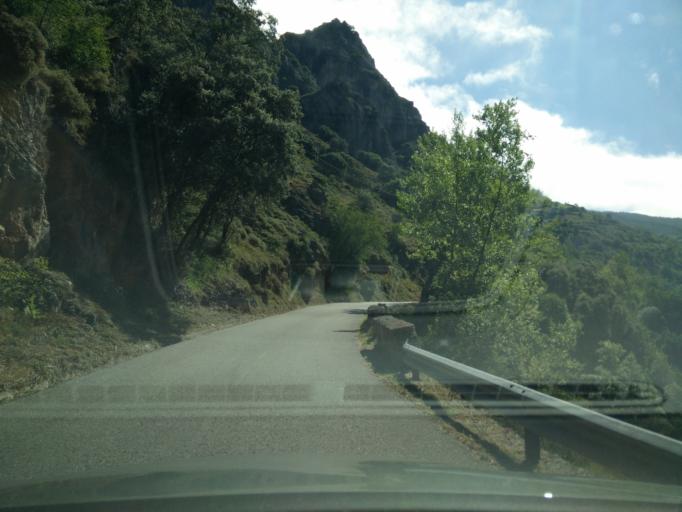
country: ES
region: Asturias
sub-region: Province of Asturias
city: Pola de Somiedo
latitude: 43.0894
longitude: -6.2480
